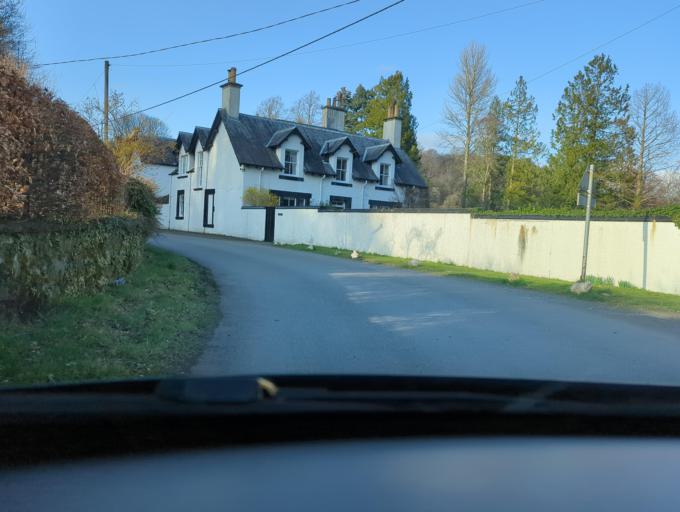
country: GB
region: Scotland
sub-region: Perth and Kinross
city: Comrie
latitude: 56.3731
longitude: -3.9967
